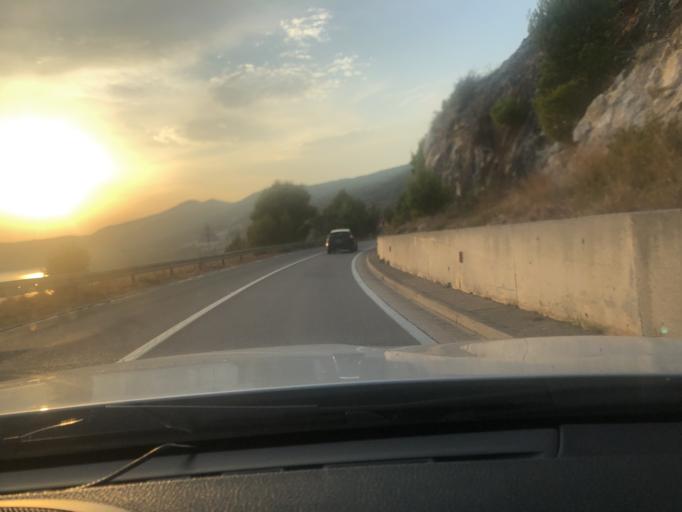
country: HR
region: Splitsko-Dalmatinska
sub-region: Grad Hvar
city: Hvar
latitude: 43.1533
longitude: 16.5112
